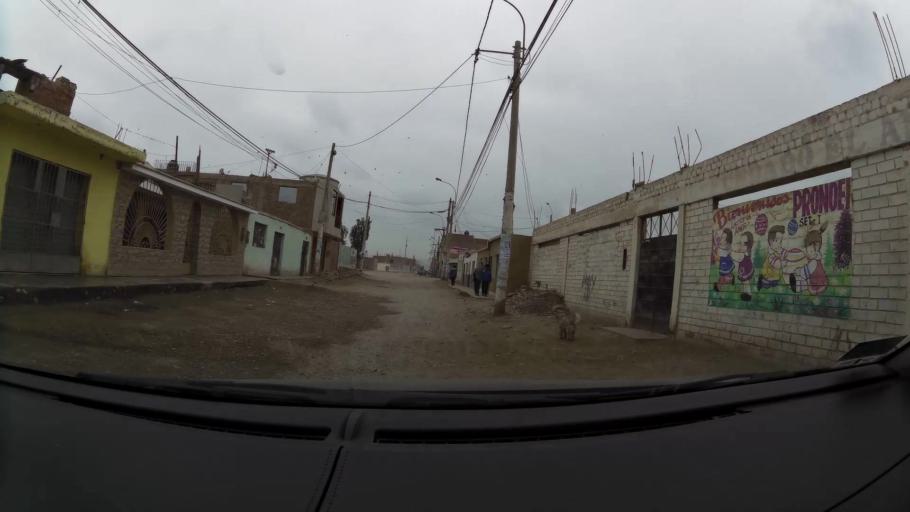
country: PE
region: Lima
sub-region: Provincia de Huaral
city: Huaral
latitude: -11.5006
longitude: -77.2317
